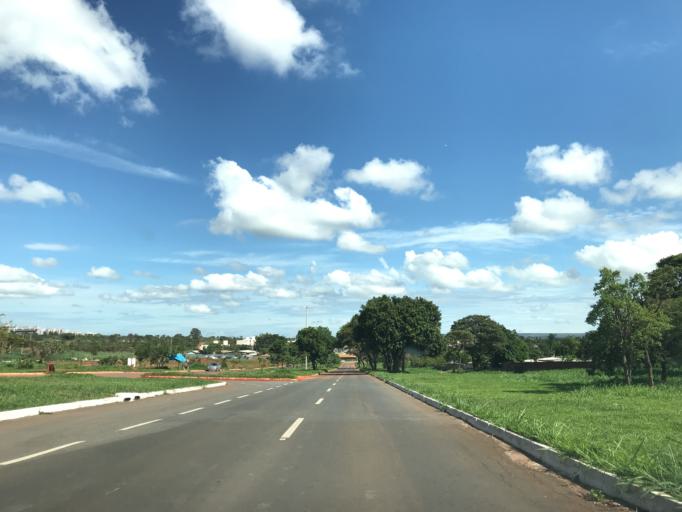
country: BR
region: Federal District
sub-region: Brasilia
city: Brasilia
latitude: -15.7621
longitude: -47.8986
